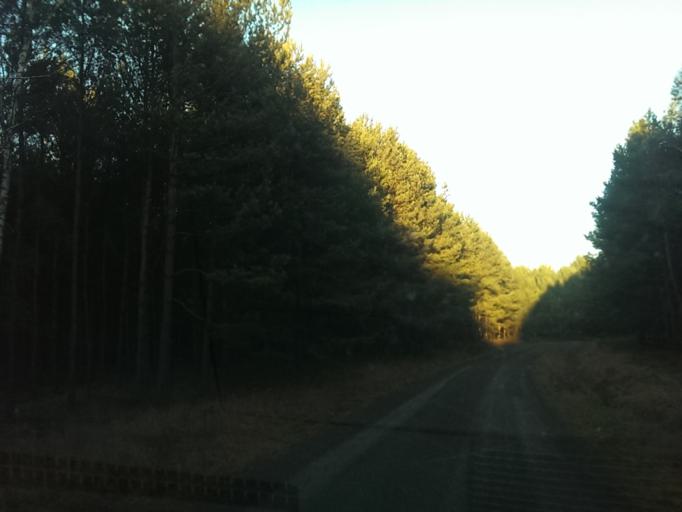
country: PL
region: Kujawsko-Pomorskie
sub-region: Powiat nakielski
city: Naklo nad Notecia
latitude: 53.0475
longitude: 17.6385
